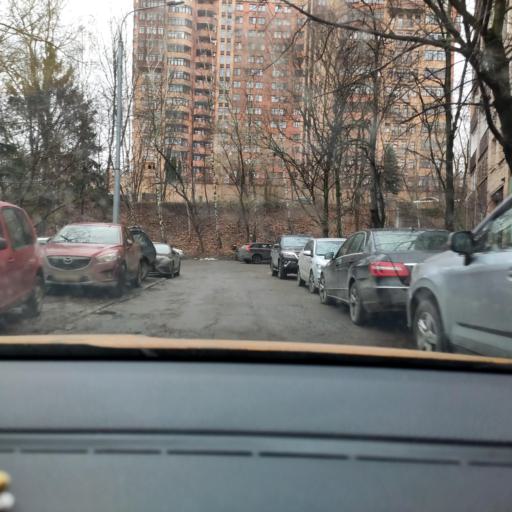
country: RU
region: Moscow
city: Vorob'yovo
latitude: 55.7167
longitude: 37.5249
